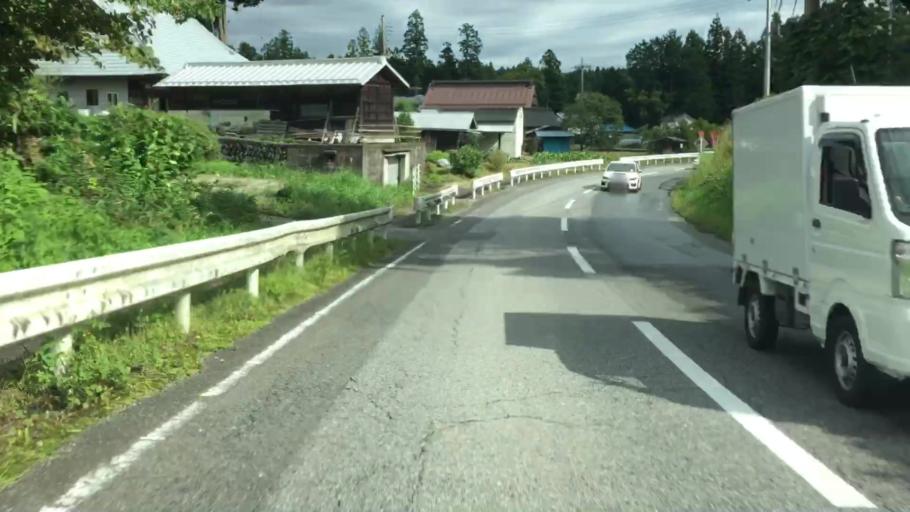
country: JP
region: Tochigi
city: Nikko
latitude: 36.7596
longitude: 139.6620
